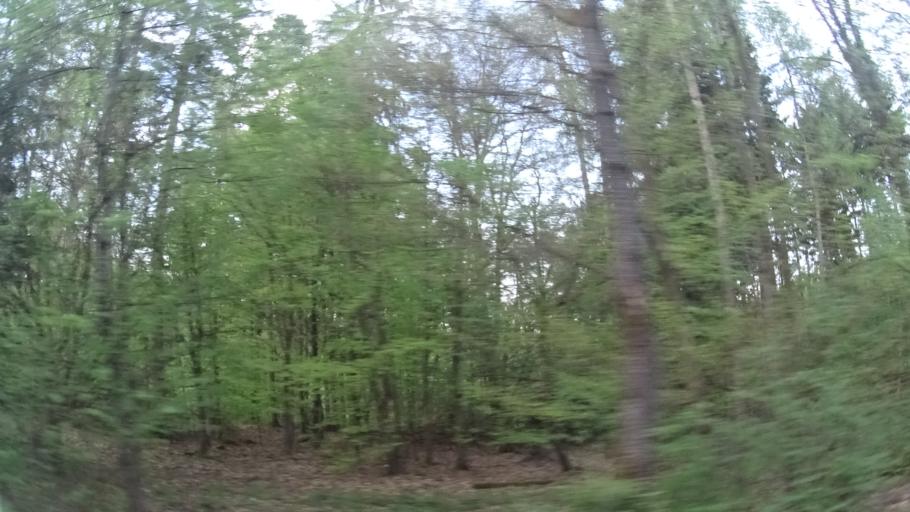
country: DE
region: Hesse
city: Neckarsteinach
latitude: 49.4243
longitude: 8.8519
